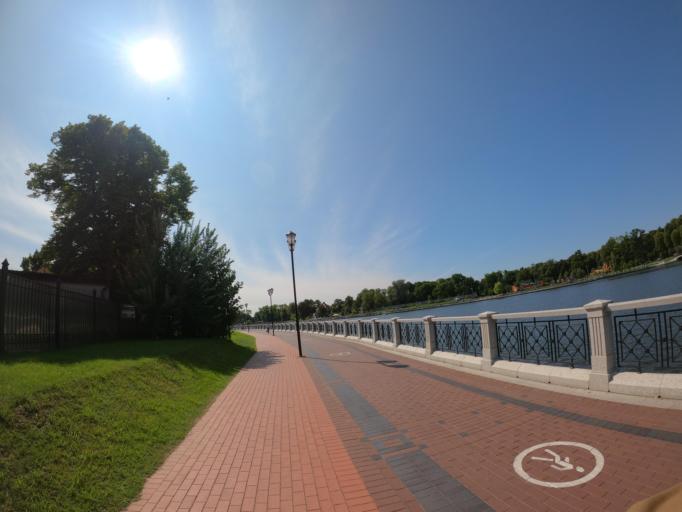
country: RU
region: Kaliningrad
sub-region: Gorod Kaliningrad
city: Kaliningrad
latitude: 54.7265
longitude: 20.5194
